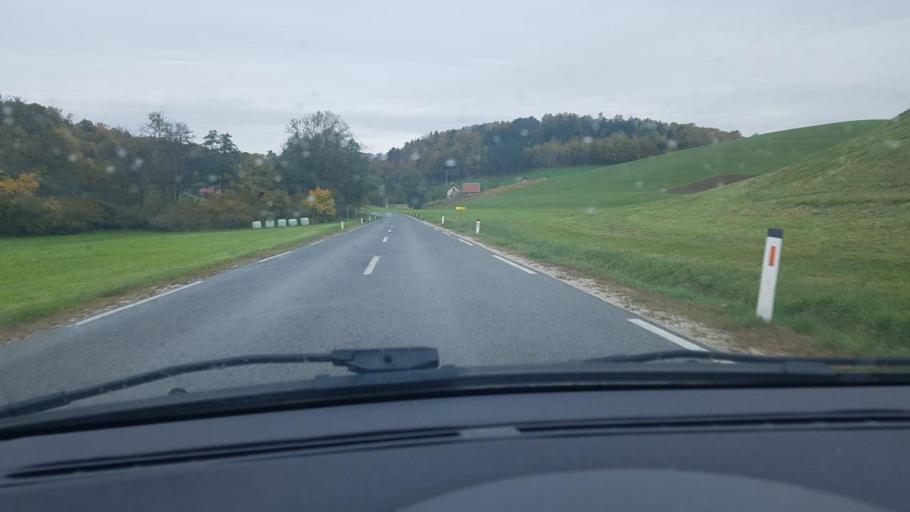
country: SI
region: Rogatec
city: Rogatec
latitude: 46.2548
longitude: 15.7021
